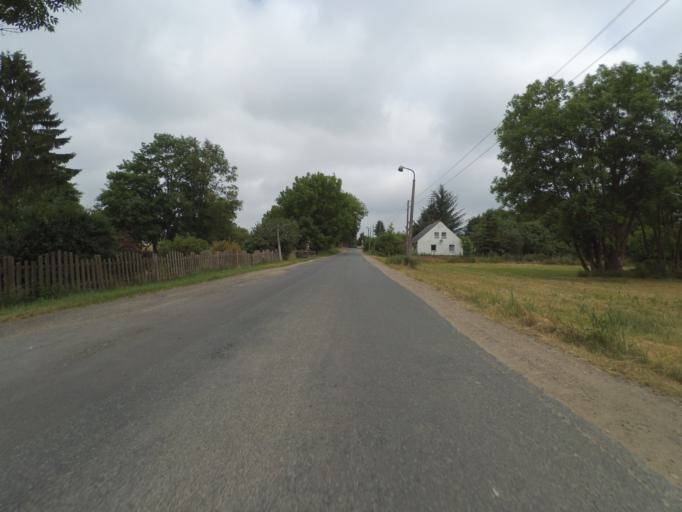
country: DE
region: Mecklenburg-Vorpommern
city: Plau am See
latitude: 53.5167
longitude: 12.2243
